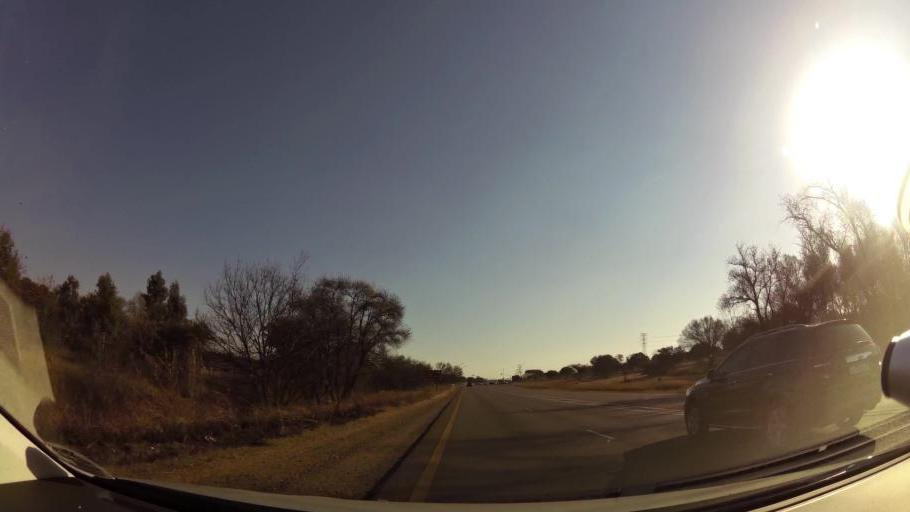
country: ZA
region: Gauteng
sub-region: City of Tshwane Metropolitan Municipality
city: Pretoria
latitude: -25.7458
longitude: 28.1355
